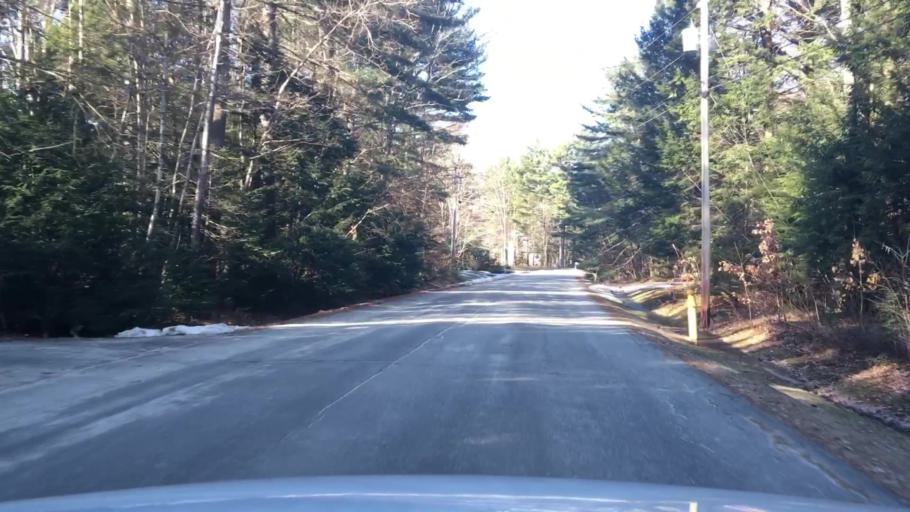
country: US
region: Maine
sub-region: Cumberland County
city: Brunswick
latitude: 43.9421
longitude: -69.9365
